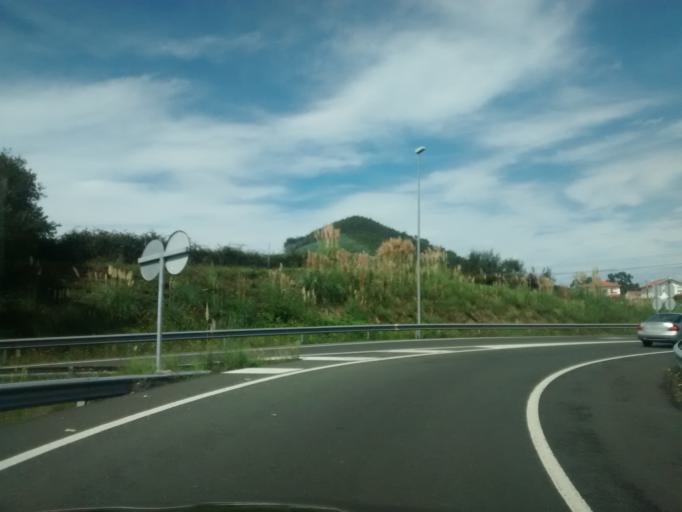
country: ES
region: Cantabria
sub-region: Provincia de Cantabria
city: Miengo
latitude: 43.4168
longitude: -3.9635
